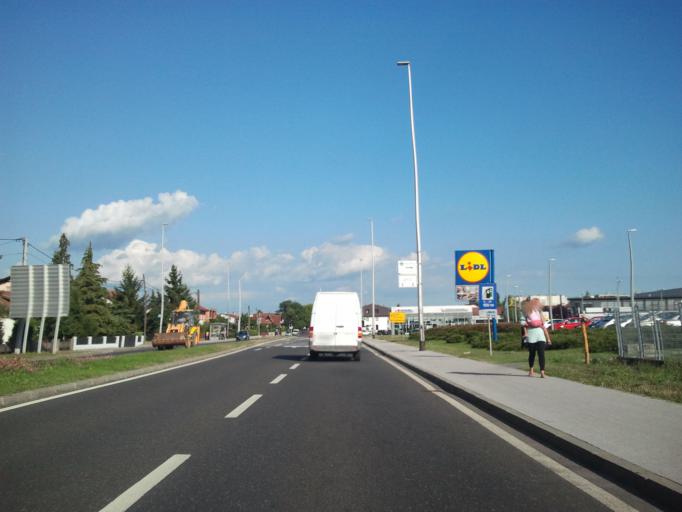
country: HR
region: Zagrebacka
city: Gradici
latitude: 45.7212
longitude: 16.0530
